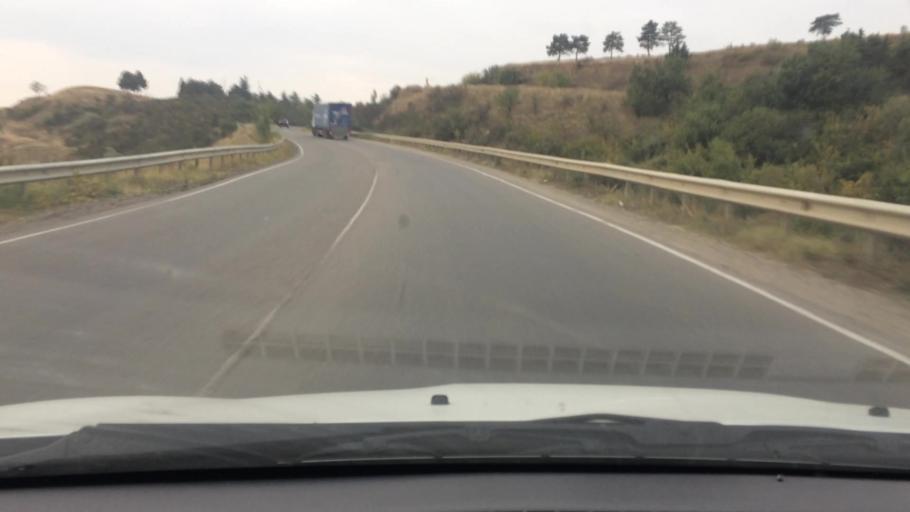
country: GE
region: T'bilisi
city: Tbilisi
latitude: 41.5958
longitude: 44.7797
